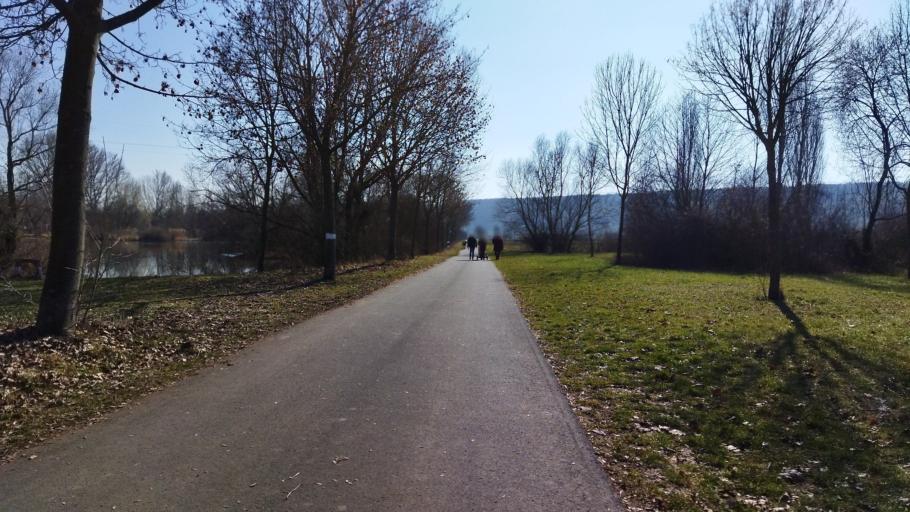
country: DE
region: Bavaria
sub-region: Regierungsbezirk Unterfranken
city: Sulzfeld am Main
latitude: 49.7015
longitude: 10.1306
